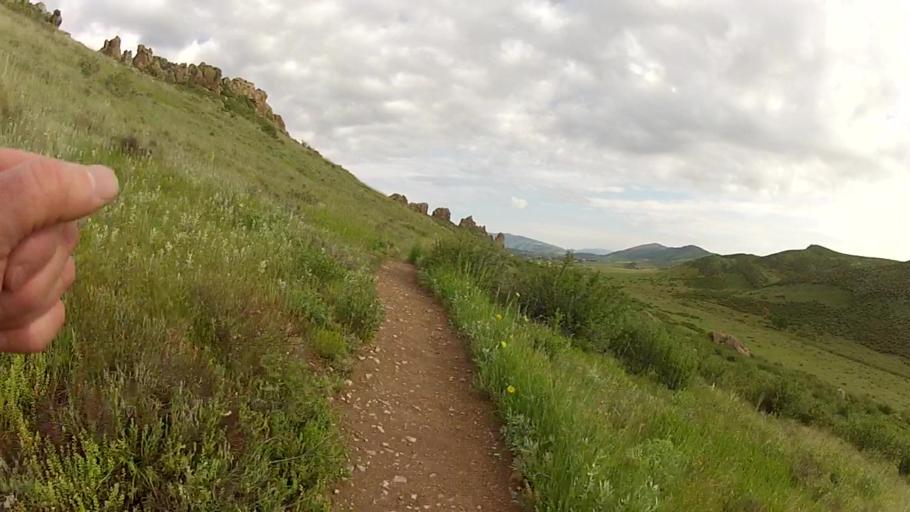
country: US
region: Colorado
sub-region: Larimer County
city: Loveland
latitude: 40.4235
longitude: -105.1624
